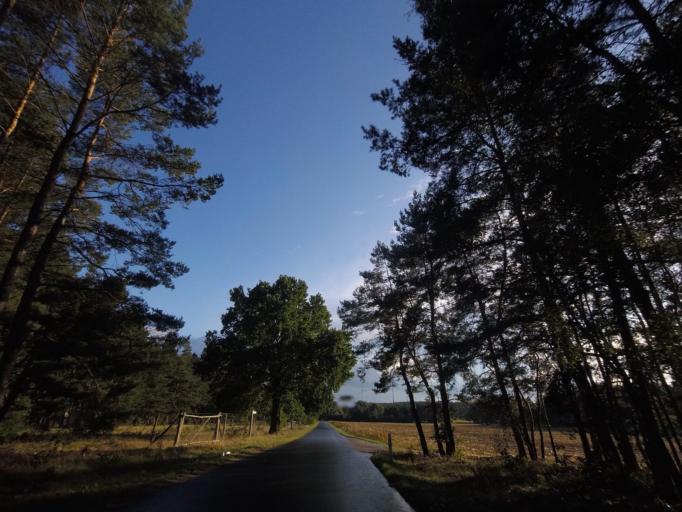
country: DE
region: Brandenburg
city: Treuenbrietzen
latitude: 52.0434
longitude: 12.8682
